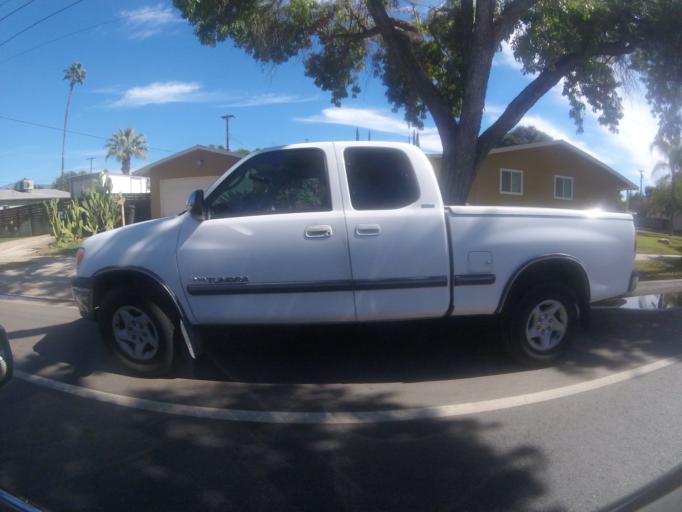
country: US
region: California
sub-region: San Bernardino County
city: Mentone
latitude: 34.0623
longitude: -117.1564
